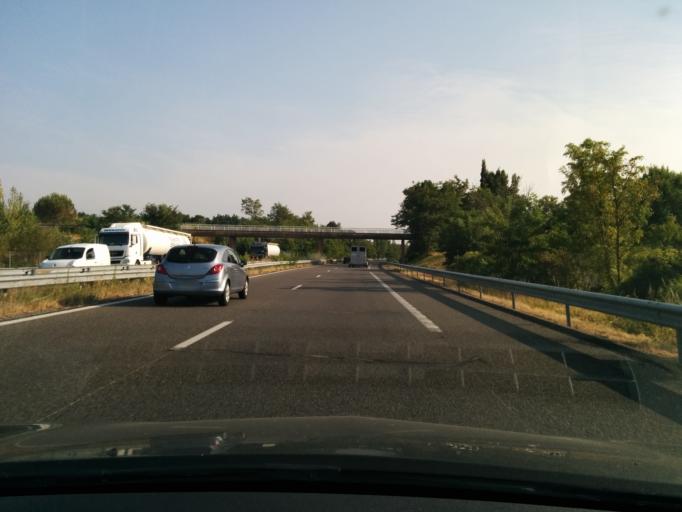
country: FR
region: Midi-Pyrenees
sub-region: Departement du Tarn
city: Montans
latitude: 43.8620
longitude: 1.8953
